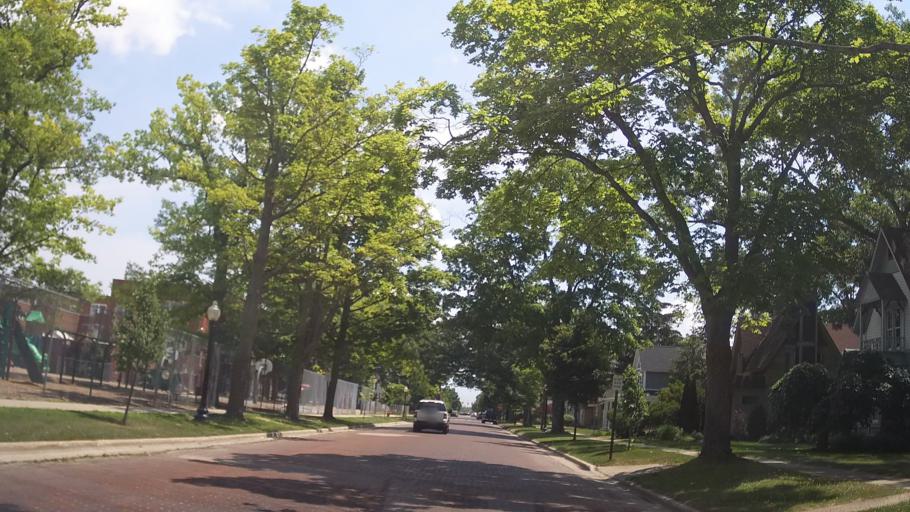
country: US
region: Michigan
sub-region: Grand Traverse County
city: Traverse City
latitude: 44.7594
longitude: -85.6281
